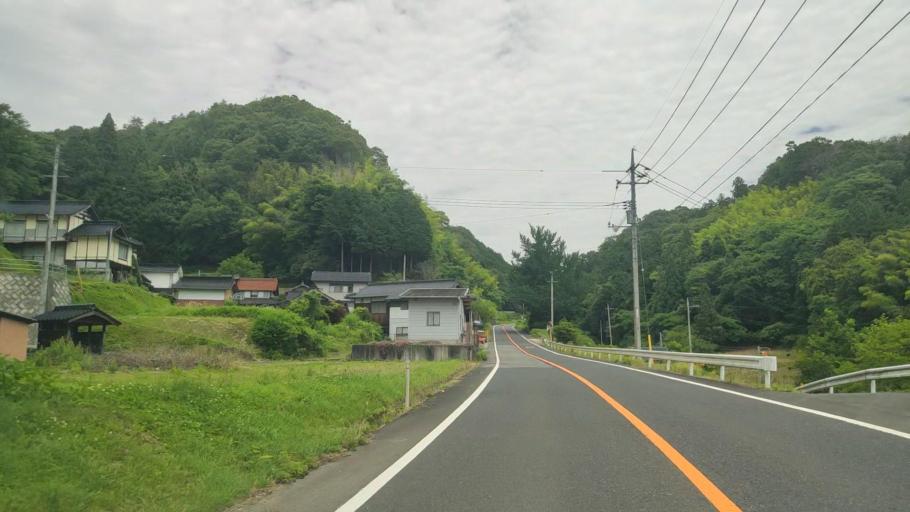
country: JP
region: Okayama
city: Tsuyama
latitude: 35.0910
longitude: 134.2606
